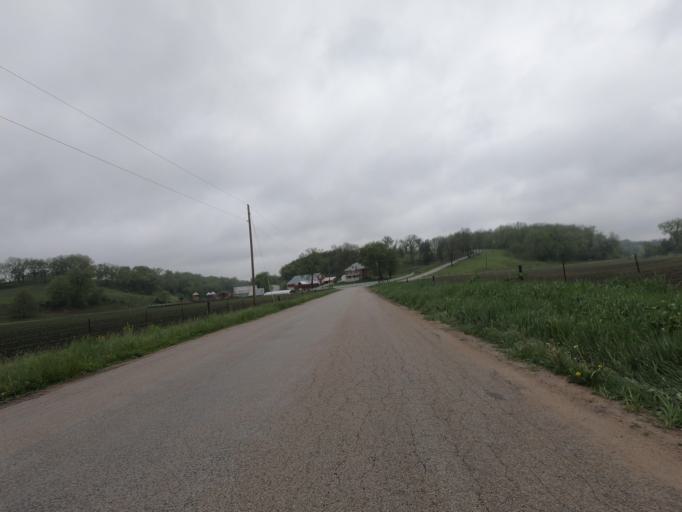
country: US
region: Wisconsin
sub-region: Grant County
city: Hazel Green
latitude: 42.4796
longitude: -90.4871
